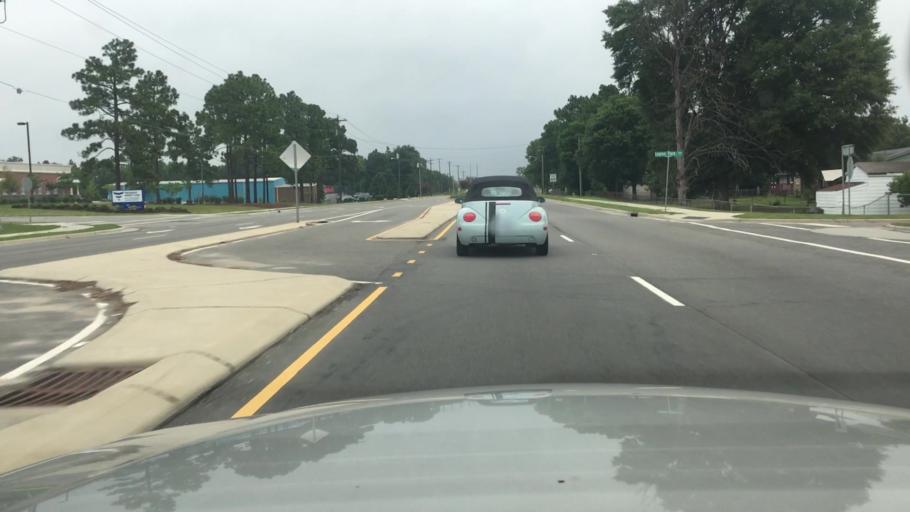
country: US
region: North Carolina
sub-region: Cumberland County
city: Fayetteville
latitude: 35.0112
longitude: -78.9098
